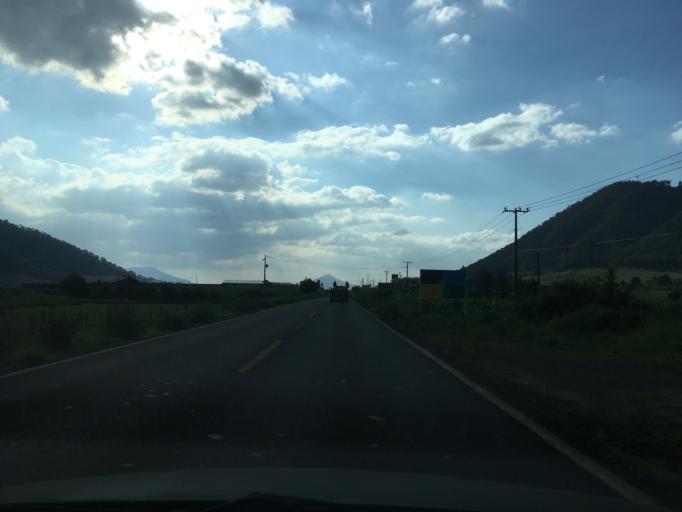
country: MX
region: Michoacan
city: Nahuatzen
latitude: 19.6642
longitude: -101.9382
